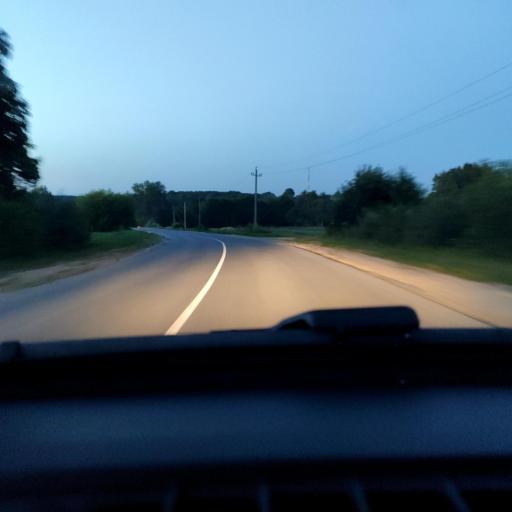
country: RU
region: Lipetsk
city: Zadonsk
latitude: 52.2893
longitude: 38.7571
